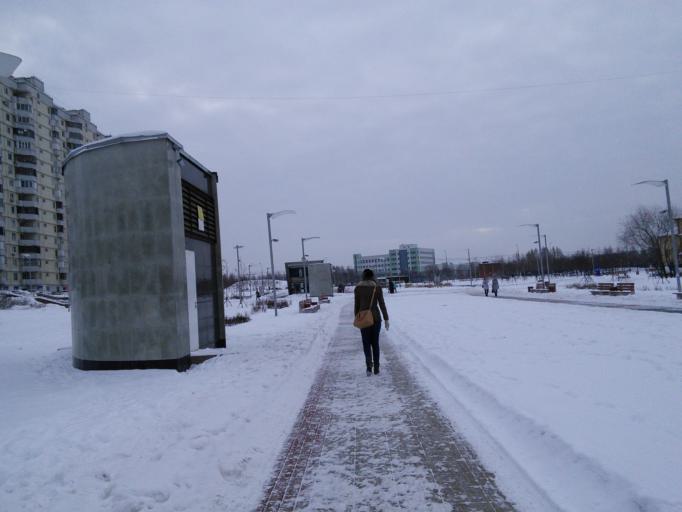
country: RU
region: Moscow
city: Brateyevo
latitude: 55.6329
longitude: 37.7660
